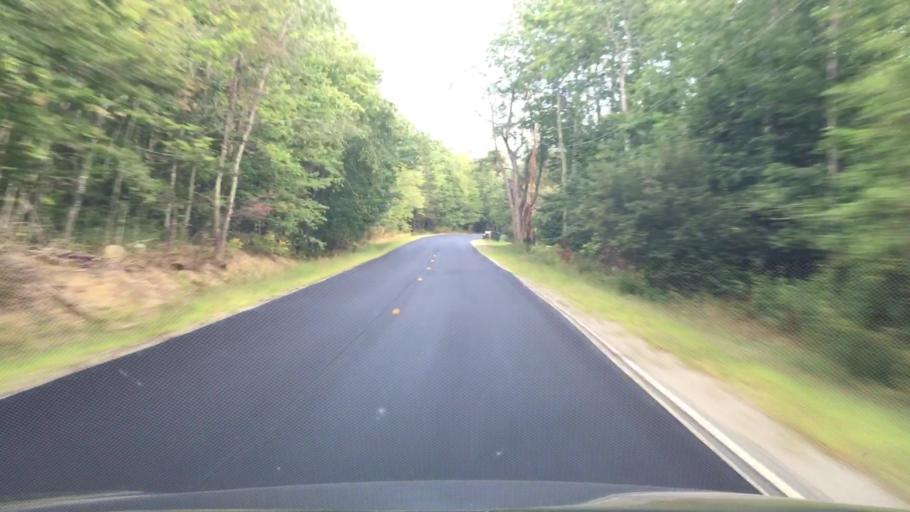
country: US
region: Maine
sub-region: Hancock County
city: Orland
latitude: 44.5446
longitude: -68.6188
